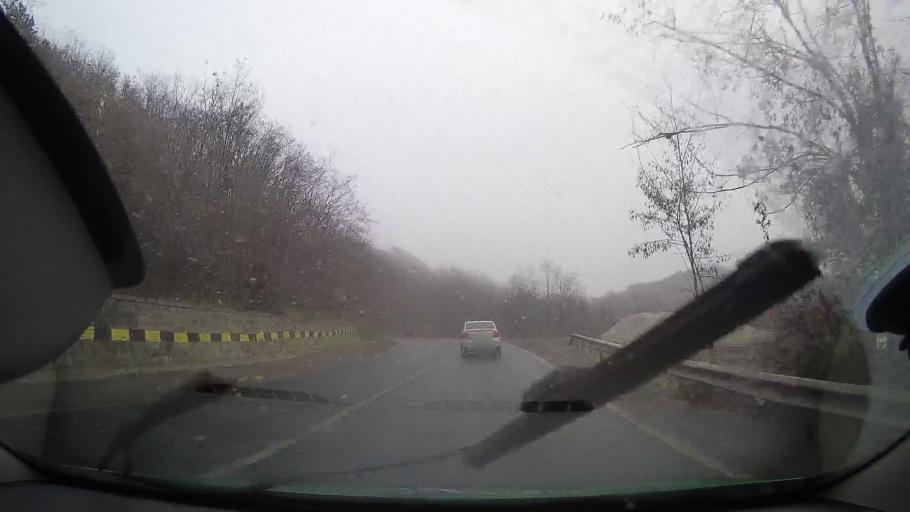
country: RO
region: Sibiu
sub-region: Municipiul Medias
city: Medias
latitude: 46.1857
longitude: 24.3311
